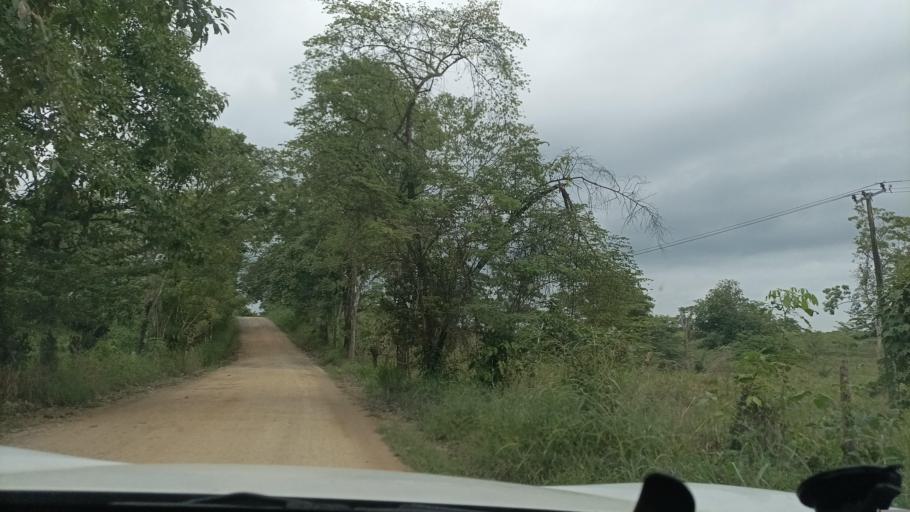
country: MX
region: Veracruz
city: Hidalgotitlan
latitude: 17.6449
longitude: -94.5096
